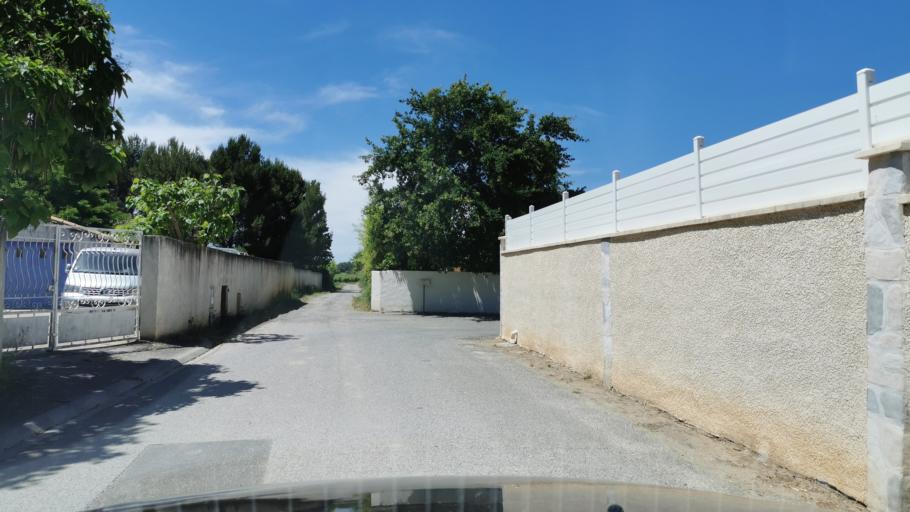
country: FR
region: Languedoc-Roussillon
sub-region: Departement de l'Aude
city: Nevian
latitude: 43.2158
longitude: 2.8970
